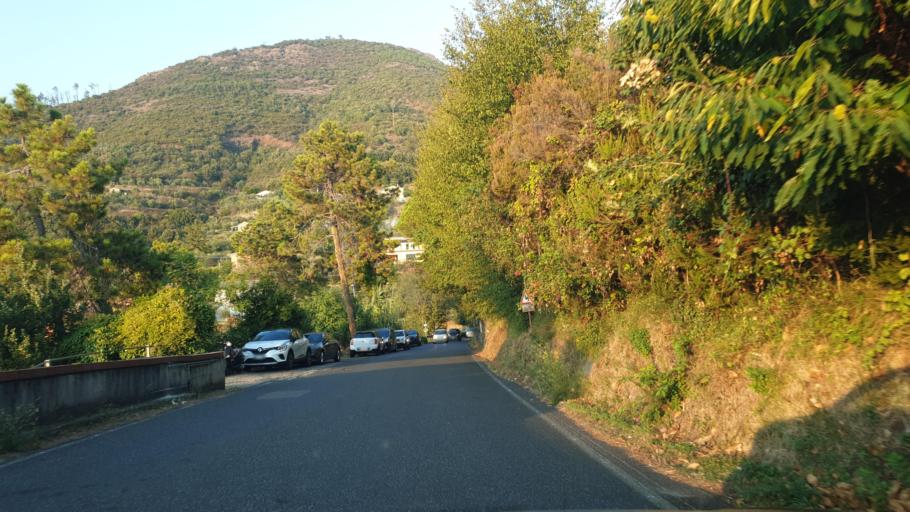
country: IT
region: Liguria
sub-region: Provincia di La Spezia
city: Bonassola
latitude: 44.1787
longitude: 9.5889
